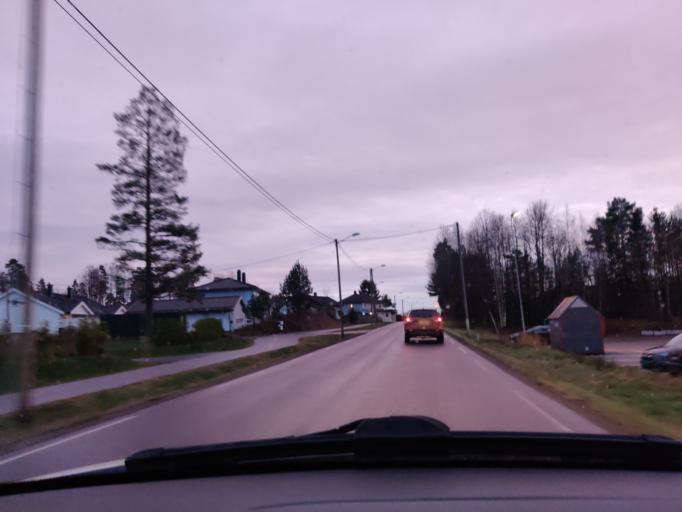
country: NO
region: Vestfold
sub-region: Tonsberg
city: Sem
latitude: 59.2636
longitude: 10.3634
